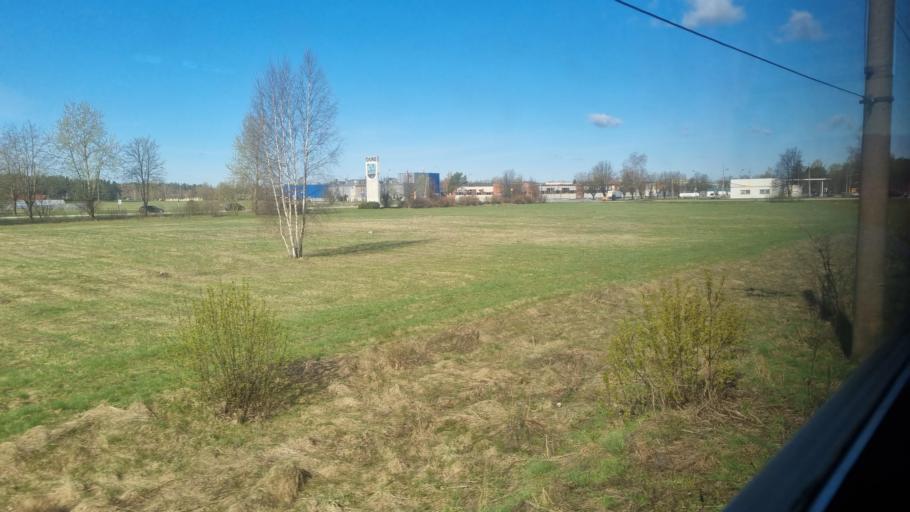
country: LV
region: Ogre
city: Ogre
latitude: 56.7928
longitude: 24.6354
